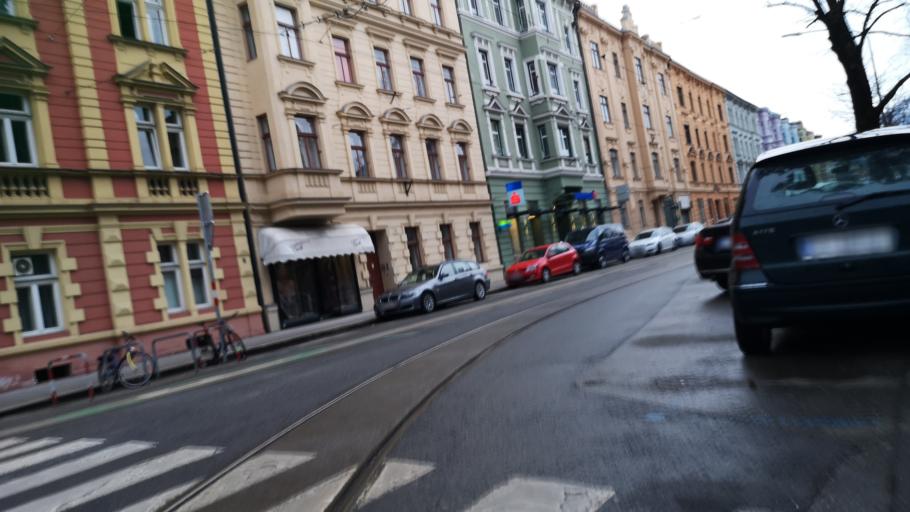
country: AT
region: Tyrol
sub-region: Innsbruck Stadt
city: Innsbruck
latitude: 47.2755
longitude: 11.4052
